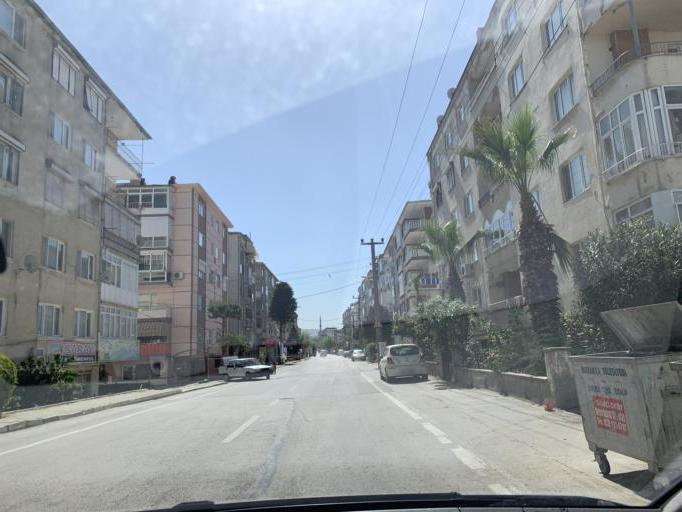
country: TR
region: Bursa
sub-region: Mudanya
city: Mudanya
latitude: 40.3615
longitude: 28.9097
